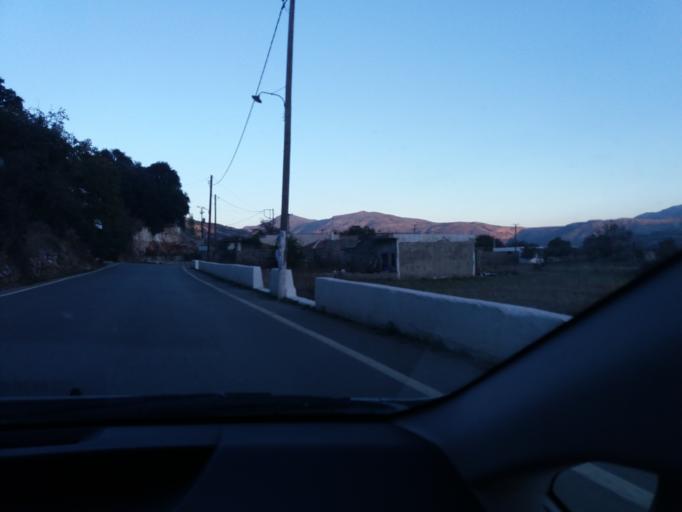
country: GR
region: Crete
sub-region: Nomos Irakleiou
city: Mokhos
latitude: 35.1968
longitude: 25.4635
